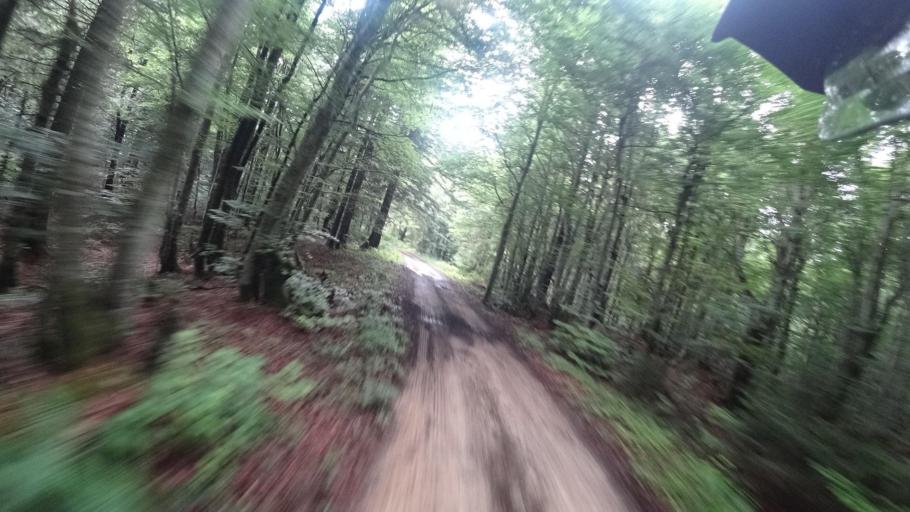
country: HR
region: Licko-Senjska
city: Jezerce
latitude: 44.7778
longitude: 15.6471
